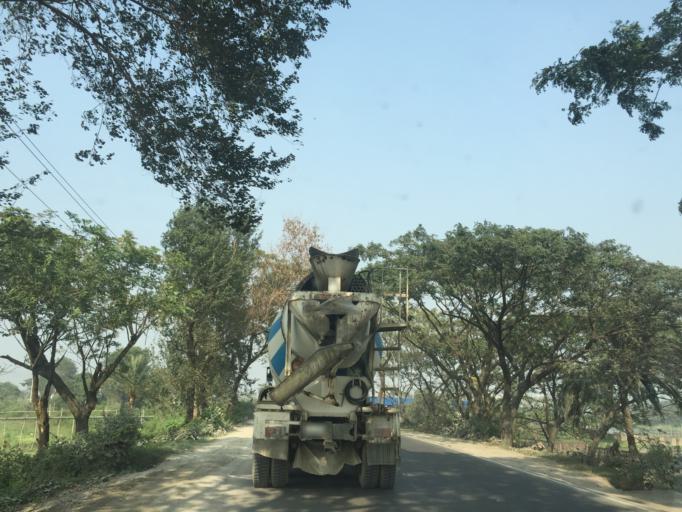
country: BD
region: Dhaka
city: Tungi
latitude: 23.8408
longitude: 90.3428
